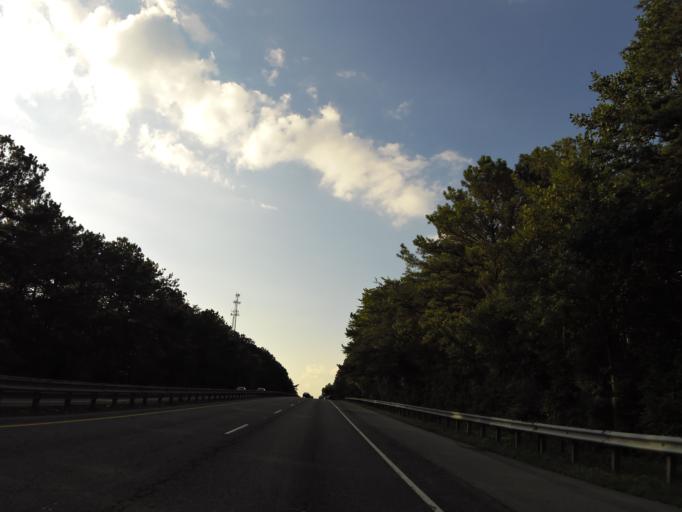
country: US
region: Tennessee
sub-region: Knox County
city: Farragut
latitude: 35.9702
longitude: -84.1771
